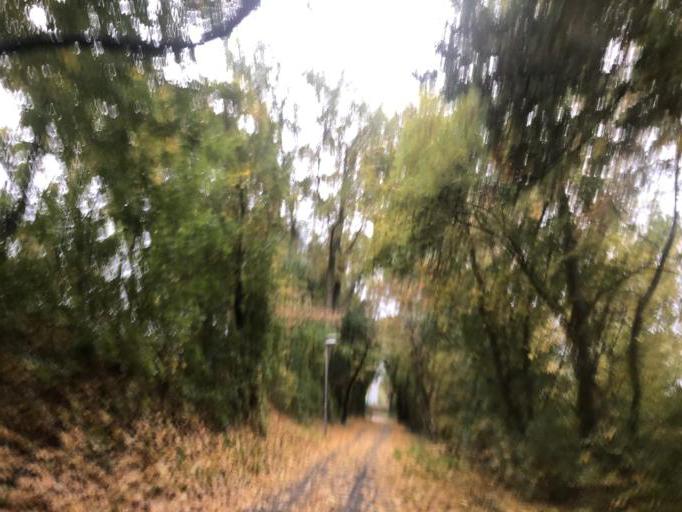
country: DE
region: Bavaria
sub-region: Regierungsbezirk Mittelfranken
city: Furth
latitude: 49.4909
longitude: 10.9864
